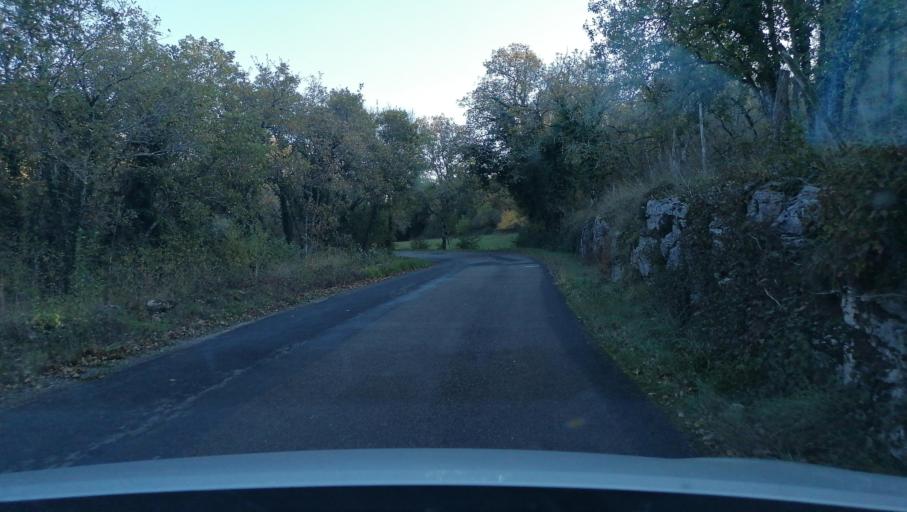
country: FR
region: Midi-Pyrenees
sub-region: Departement du Lot
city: Vayrac
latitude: 44.8760
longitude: 1.6591
